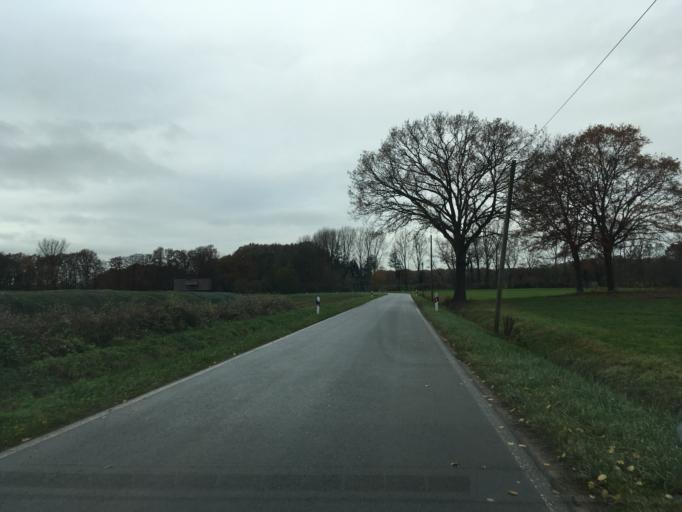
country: DE
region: North Rhine-Westphalia
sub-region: Regierungsbezirk Munster
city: Gescher
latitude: 51.9820
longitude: 6.9902
